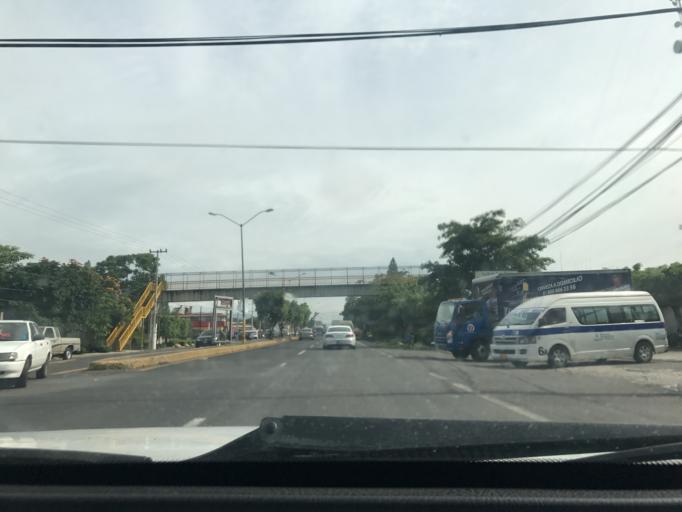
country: MX
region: Morelos
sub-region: Cuautla
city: Tierra Larga (Campo Nuevo)
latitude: 18.8719
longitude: -98.9257
